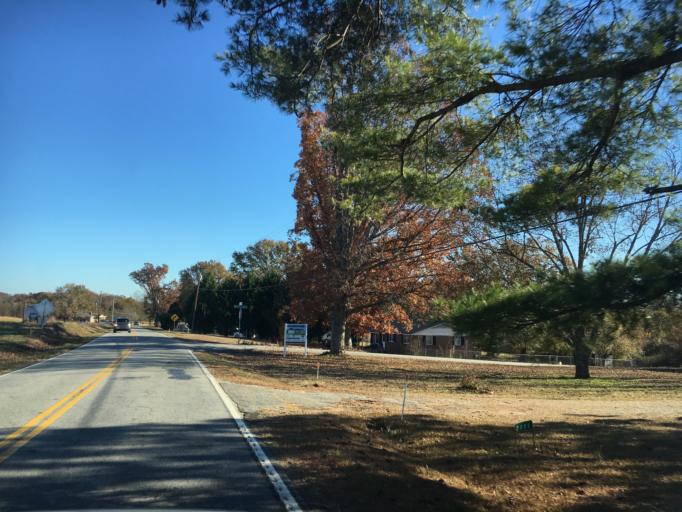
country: US
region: South Carolina
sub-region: Spartanburg County
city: Duncan
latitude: 35.0105
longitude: -82.1800
